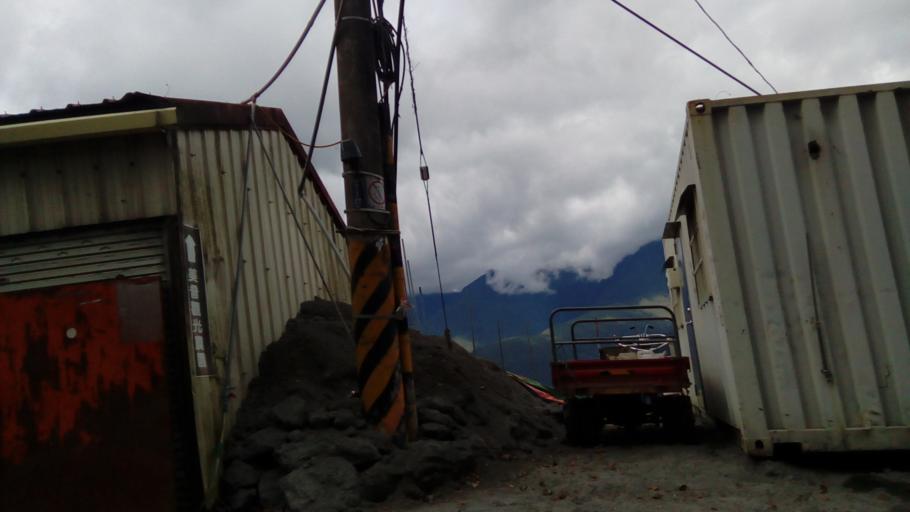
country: TW
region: Taiwan
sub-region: Nantou
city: Puli
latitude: 24.2565
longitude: 121.2547
